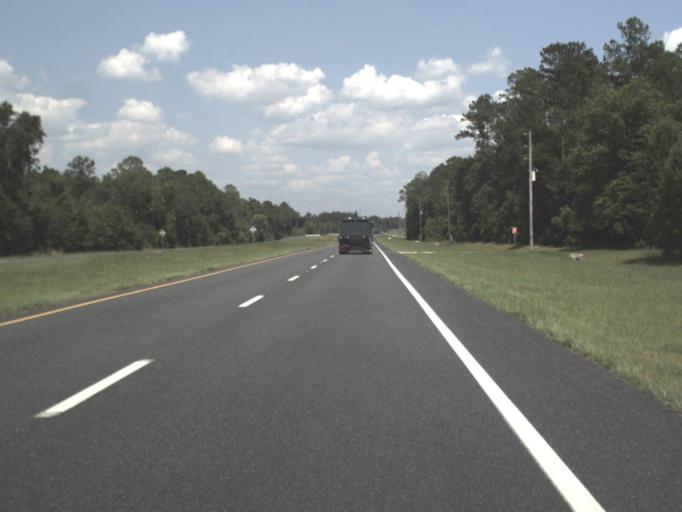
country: US
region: Florida
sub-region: Alachua County
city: Hawthorne
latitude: 29.6005
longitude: -82.1506
